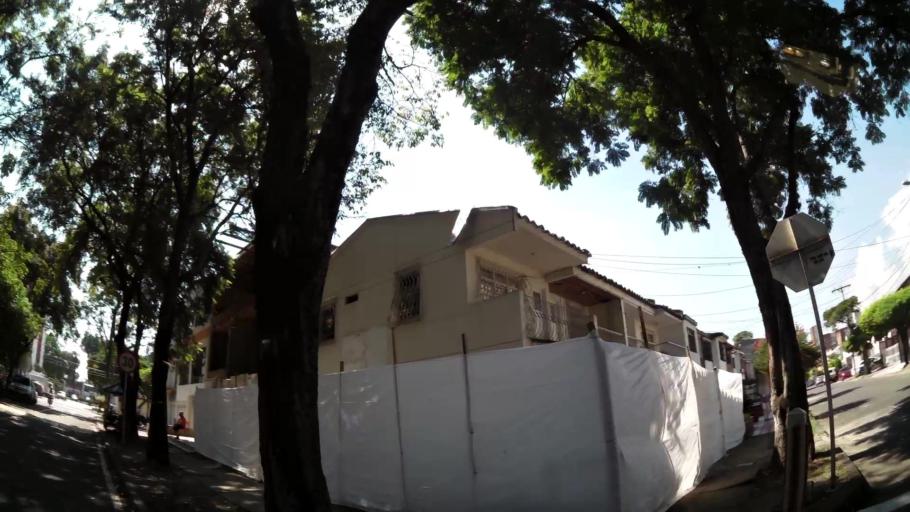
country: CO
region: Valle del Cauca
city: Cali
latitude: 3.4271
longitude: -76.5297
